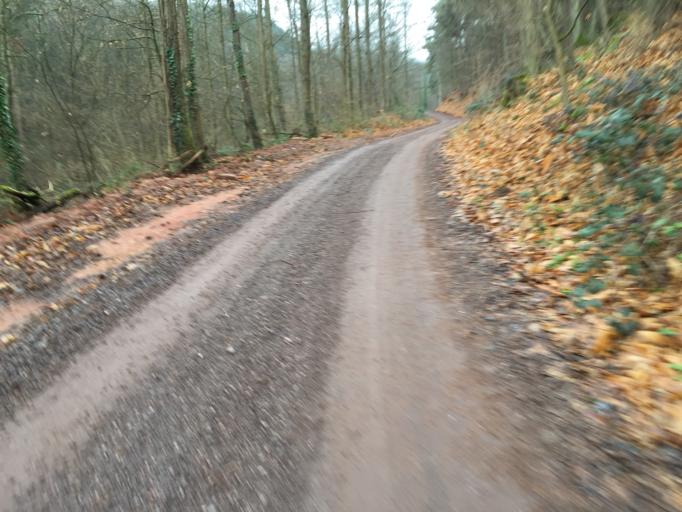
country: DE
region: Rheinland-Pfalz
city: Sankt Martin
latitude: 49.3175
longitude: 8.1053
